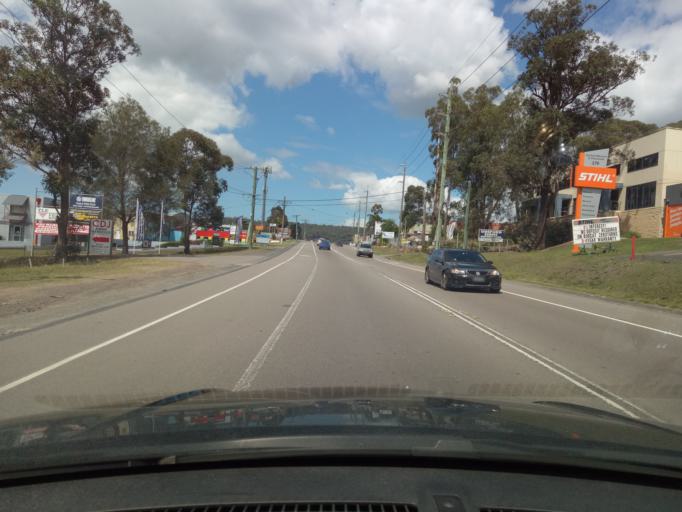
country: AU
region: New South Wales
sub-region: Gosford Shire
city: Point Clare
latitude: -33.4207
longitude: 151.3196
